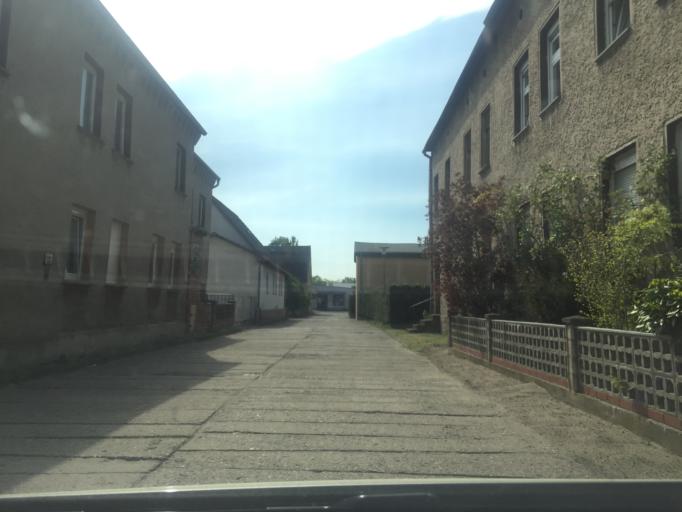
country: DE
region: Mecklenburg-Vorpommern
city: Torgelow
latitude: 53.6292
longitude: 14.0170
